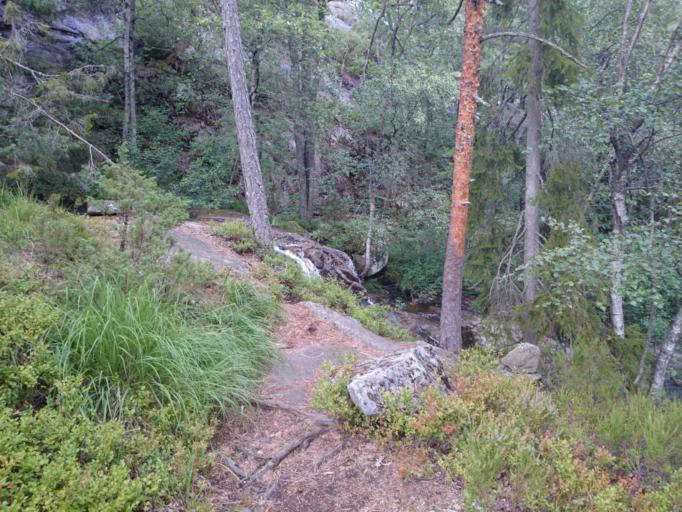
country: NO
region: Aust-Agder
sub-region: Amli
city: Amli
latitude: 58.7692
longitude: 8.4655
